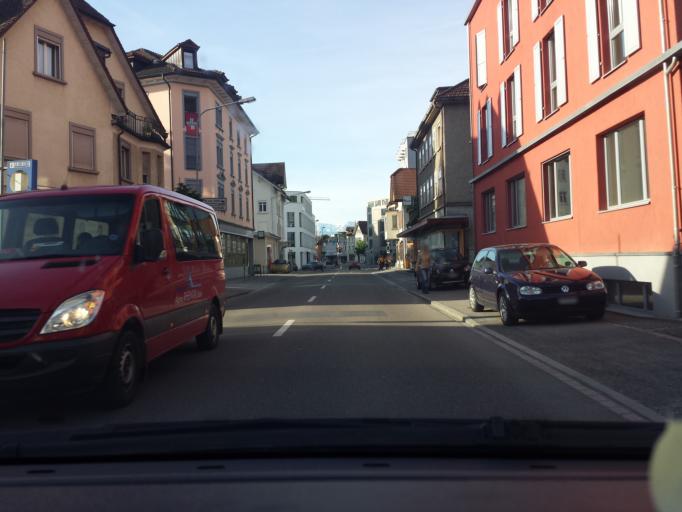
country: CH
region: Appenzell Innerrhoden
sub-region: Appenzell Inner Rhodes
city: Balgach
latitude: 47.4122
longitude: 9.6254
